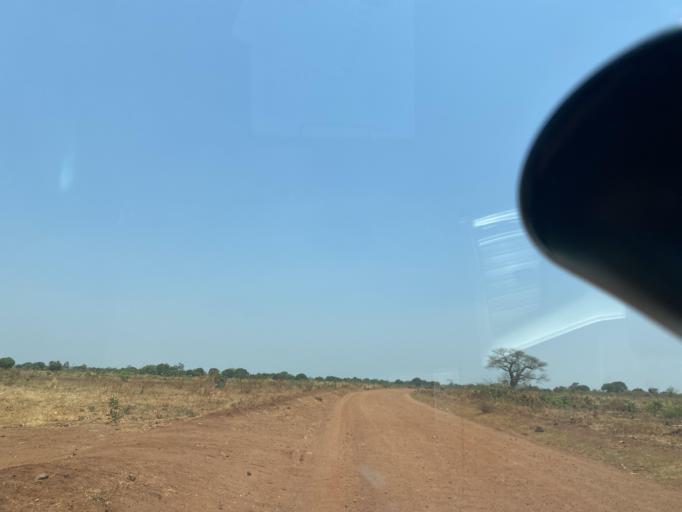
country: ZM
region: Southern
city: Nakambala
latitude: -15.5035
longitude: 27.9200
